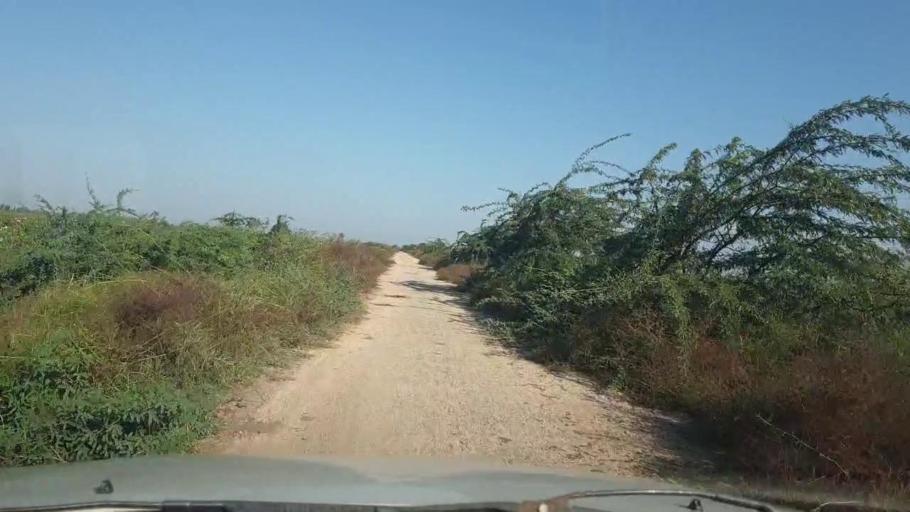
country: PK
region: Sindh
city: Chuhar Jamali
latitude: 24.5518
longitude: 67.9092
